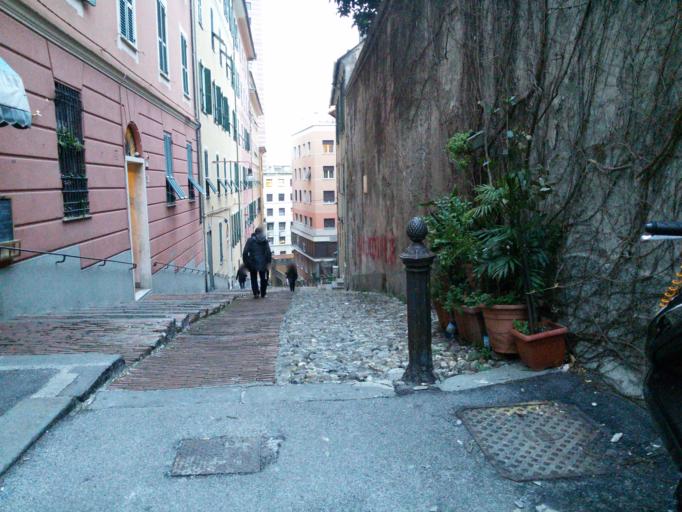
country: IT
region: Liguria
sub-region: Provincia di Genova
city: San Teodoro
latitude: 44.4039
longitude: 8.9375
